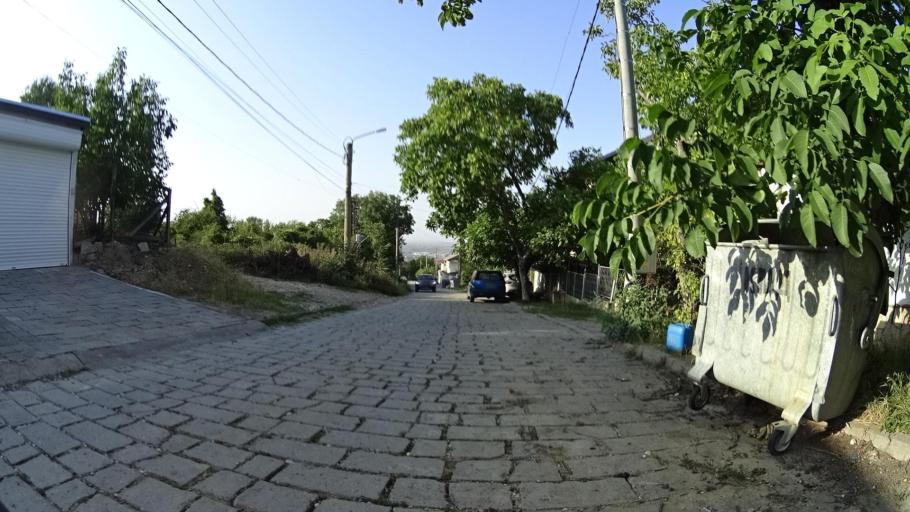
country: BG
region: Plovdiv
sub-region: Obshtina Plovdiv
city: Plovdiv
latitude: 42.0620
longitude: 24.6996
